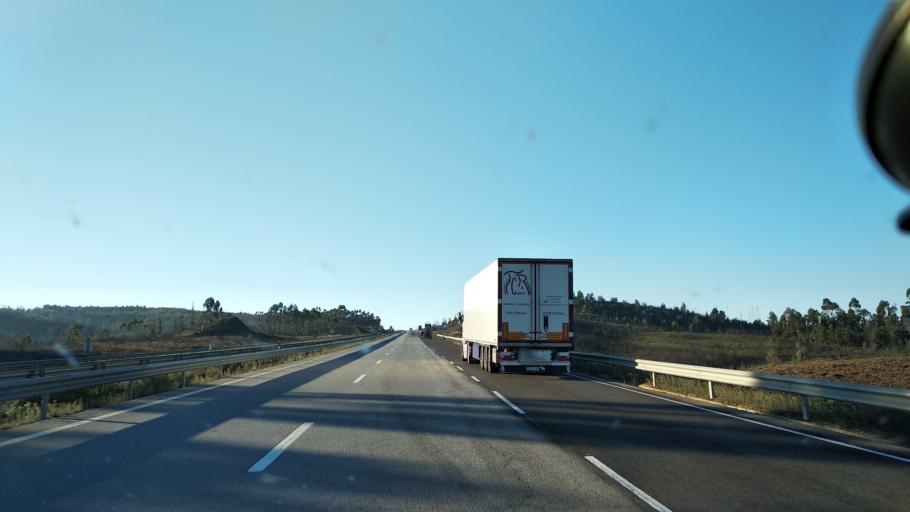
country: PT
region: Portalegre
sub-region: Gaviao
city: Gaviao
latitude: 39.5336
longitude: -7.9078
